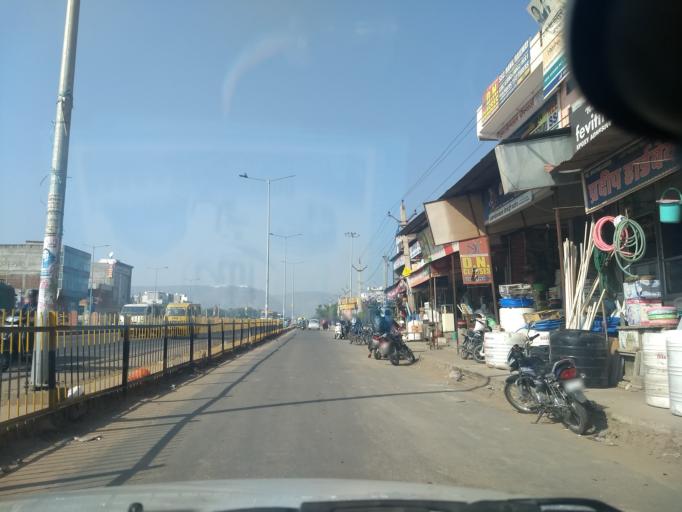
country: IN
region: Rajasthan
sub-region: Jaipur
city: Jaipur
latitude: 26.8880
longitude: 75.8856
